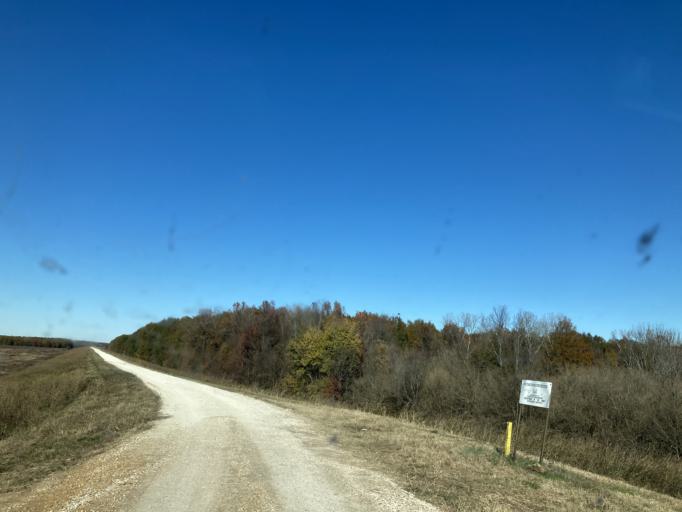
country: US
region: Mississippi
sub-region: Sharkey County
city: Rolling Fork
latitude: 32.7030
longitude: -90.6805
